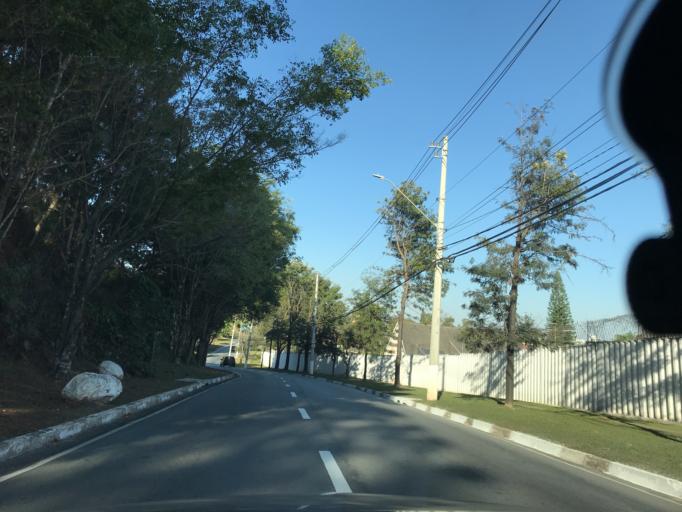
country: BR
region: Sao Paulo
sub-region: Barueri
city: Barueri
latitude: -23.4643
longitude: -46.8743
